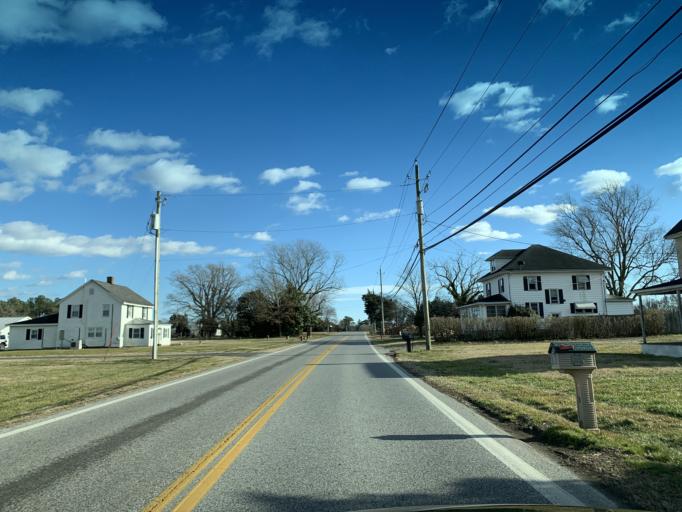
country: US
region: Maryland
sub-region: Worcester County
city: Berlin
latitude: 38.3208
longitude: -75.2021
